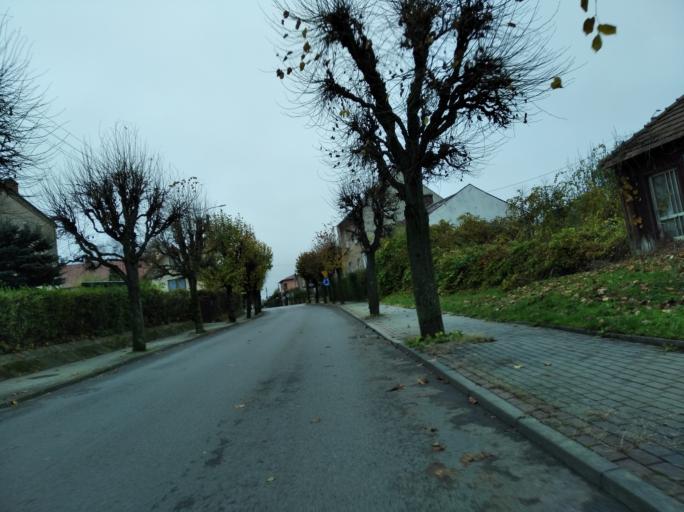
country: PL
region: Subcarpathian Voivodeship
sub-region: Krosno
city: Krosno
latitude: 49.6937
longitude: 21.7596
